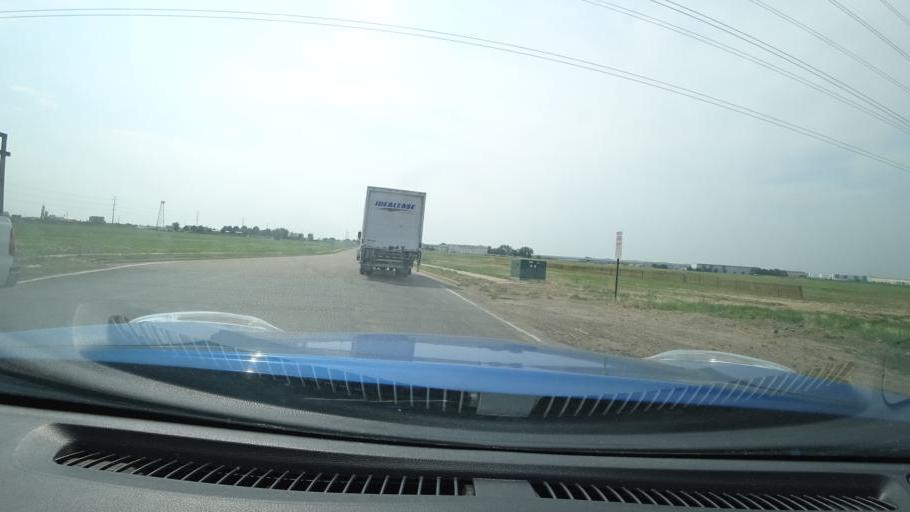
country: US
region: Colorado
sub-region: Adams County
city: Aurora
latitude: 39.7568
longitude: -104.7347
